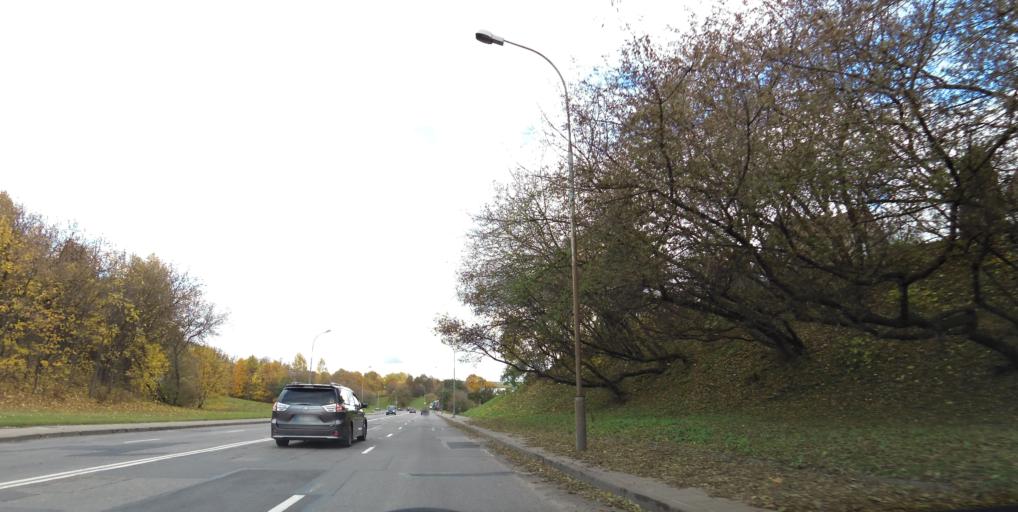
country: LT
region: Vilnius County
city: Rasos
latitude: 54.6635
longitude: 25.3033
